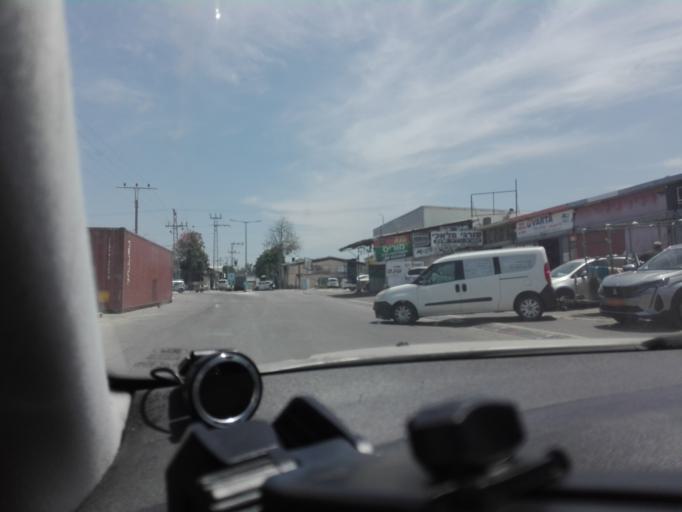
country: IL
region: Central District
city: Bene 'Ayish
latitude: 31.7338
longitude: 34.7551
